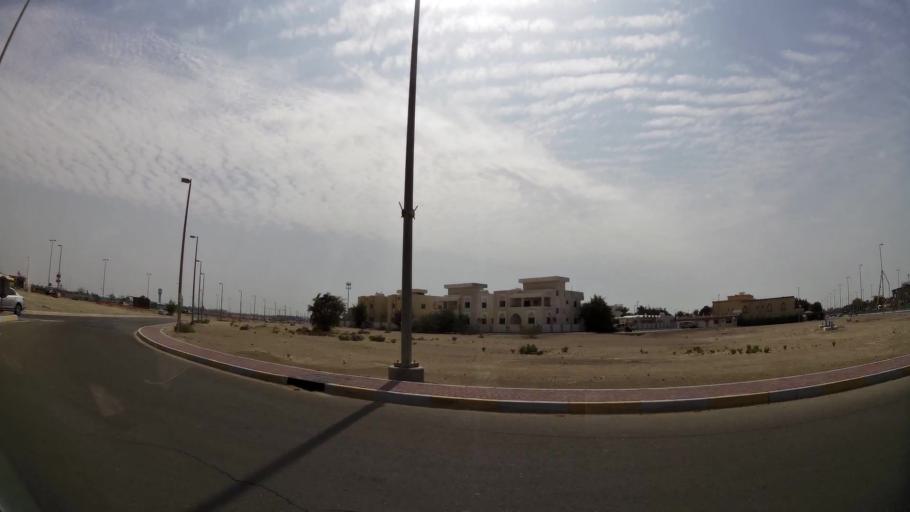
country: AE
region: Abu Dhabi
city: Abu Dhabi
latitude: 24.5495
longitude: 54.6838
